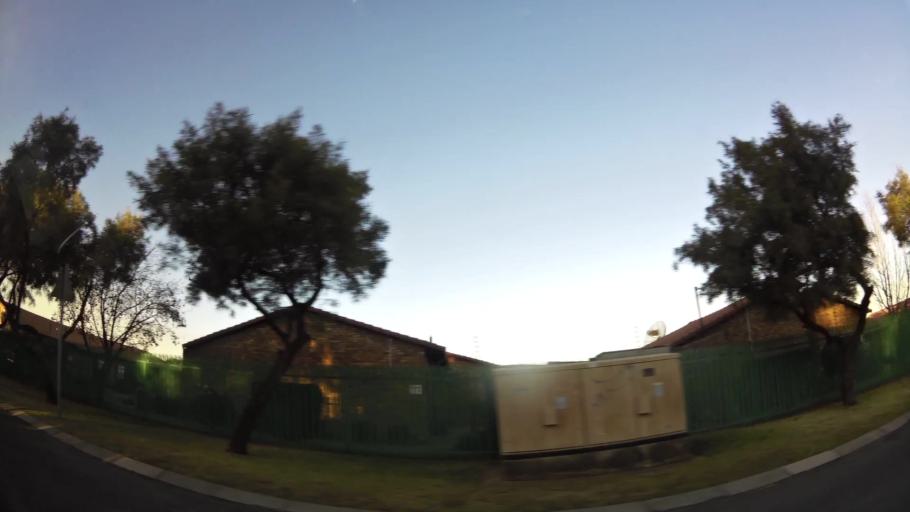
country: ZA
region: Gauteng
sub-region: City of Johannesburg Metropolitan Municipality
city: Roodepoort
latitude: -26.1488
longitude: 27.8873
